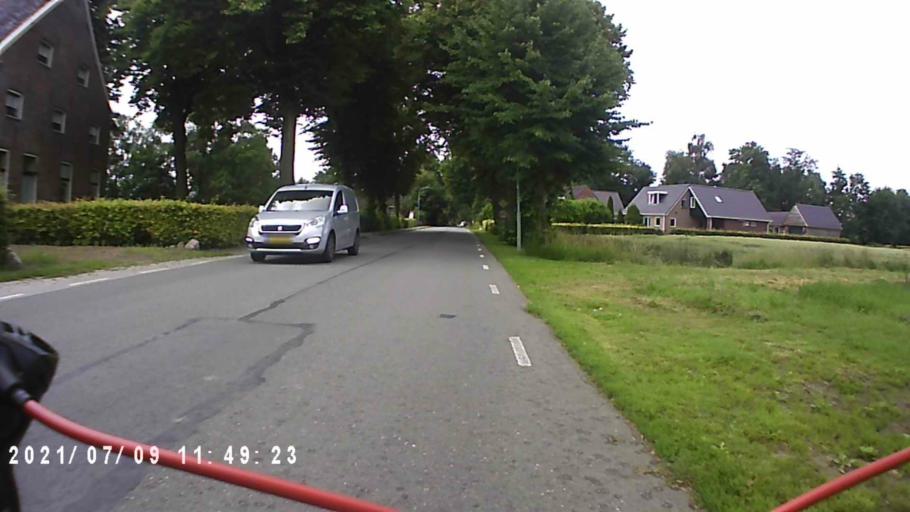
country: NL
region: Groningen
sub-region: Gemeente Veendam
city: Veendam
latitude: 53.1834
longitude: 6.8749
